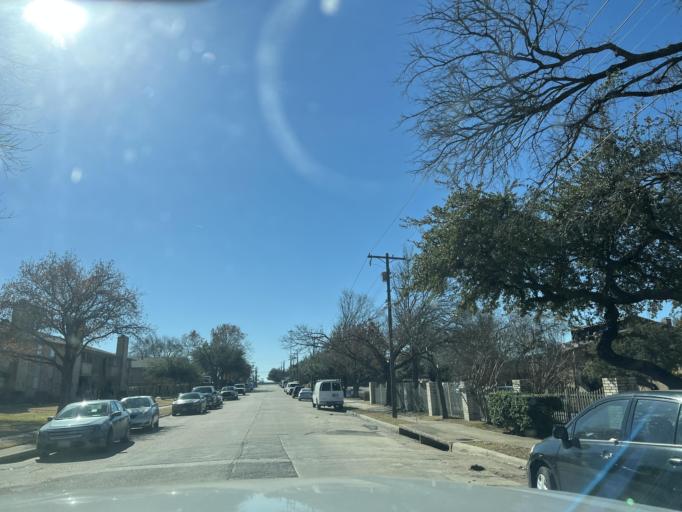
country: US
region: Texas
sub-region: Dallas County
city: Richardson
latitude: 32.9425
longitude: -96.7481
